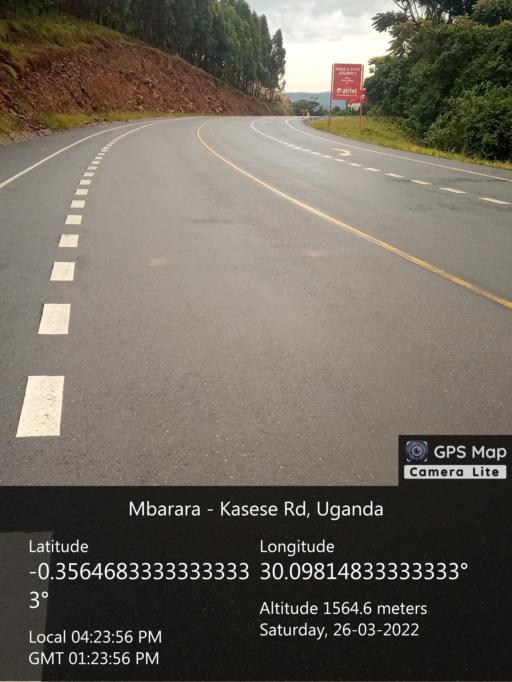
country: UG
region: Western Region
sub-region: Rubirizi District
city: Rubirizi
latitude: -0.3565
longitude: 30.0982
